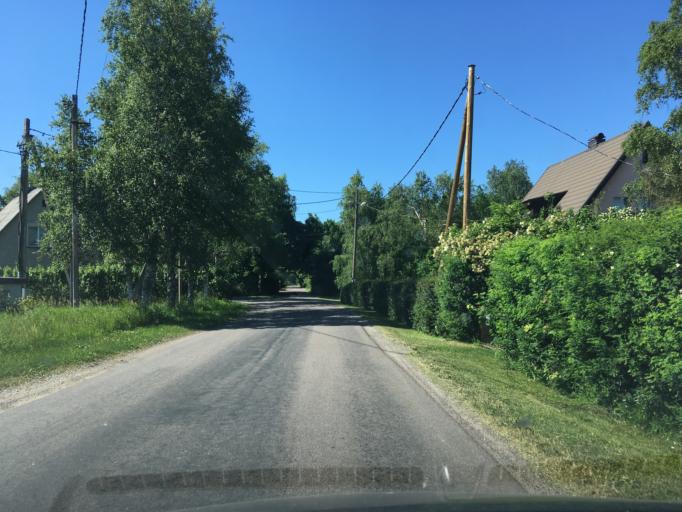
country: EE
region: Harju
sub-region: Raasiku vald
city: Raasiku
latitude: 59.3658
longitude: 25.1847
